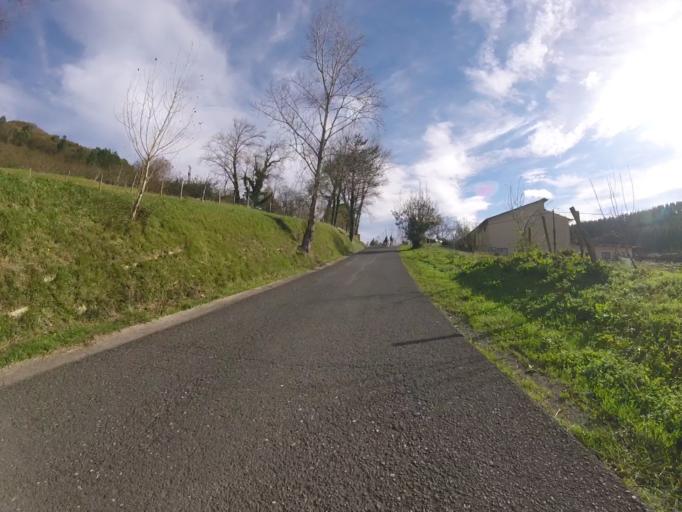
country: ES
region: Basque Country
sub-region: Provincia de Guipuzcoa
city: Orio
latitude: 43.2847
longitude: -2.1082
